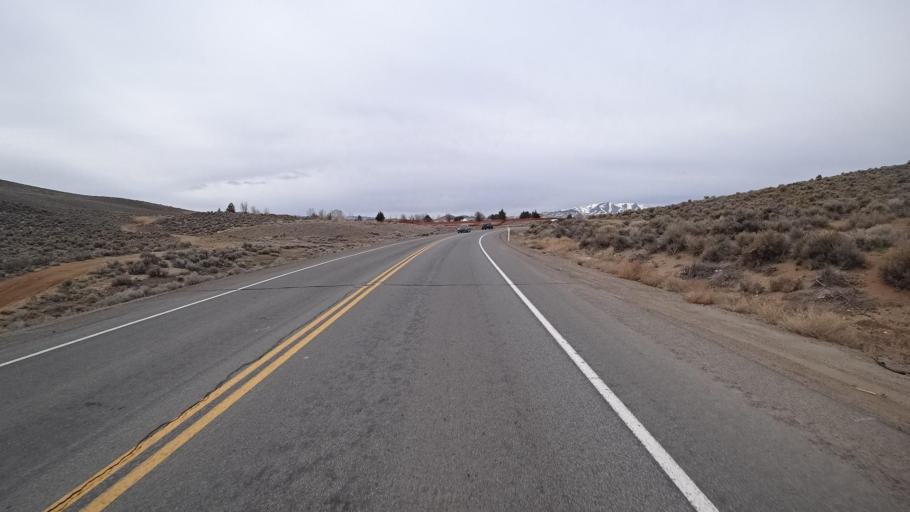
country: US
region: Nevada
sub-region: Washoe County
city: Sun Valley
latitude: 39.6081
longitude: -119.7506
